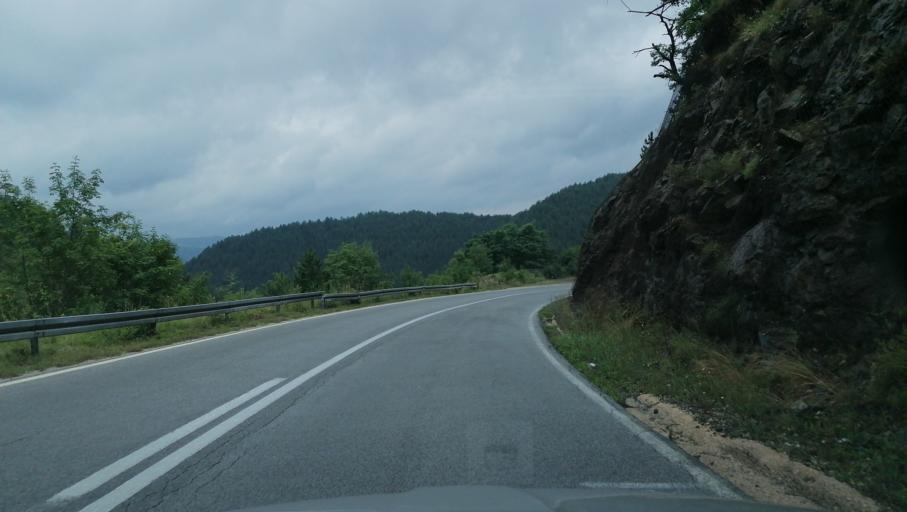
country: RS
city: Durici
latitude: 43.8218
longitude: 19.5137
